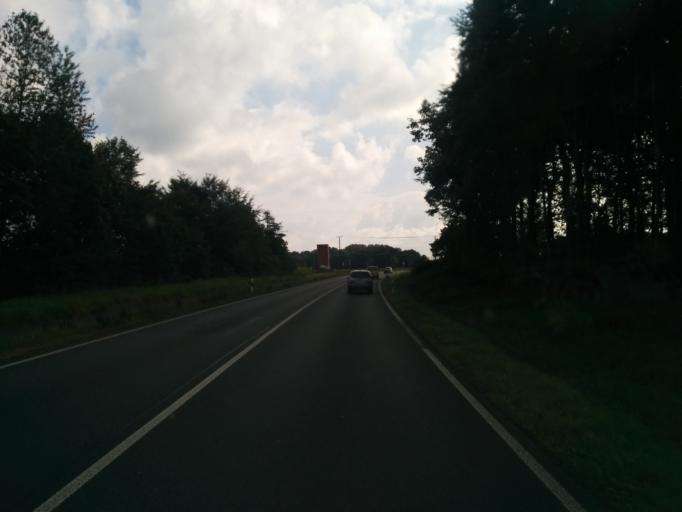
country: DE
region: North Rhine-Westphalia
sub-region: Regierungsbezirk Munster
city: Dulmen
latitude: 51.8570
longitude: 7.2471
